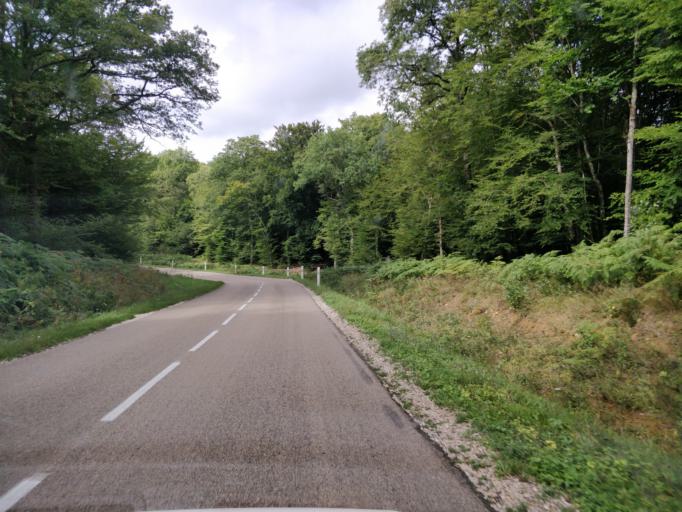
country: FR
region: Bourgogne
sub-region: Departement de l'Yonne
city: Saint-Florentin
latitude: 48.1062
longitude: 3.6729
